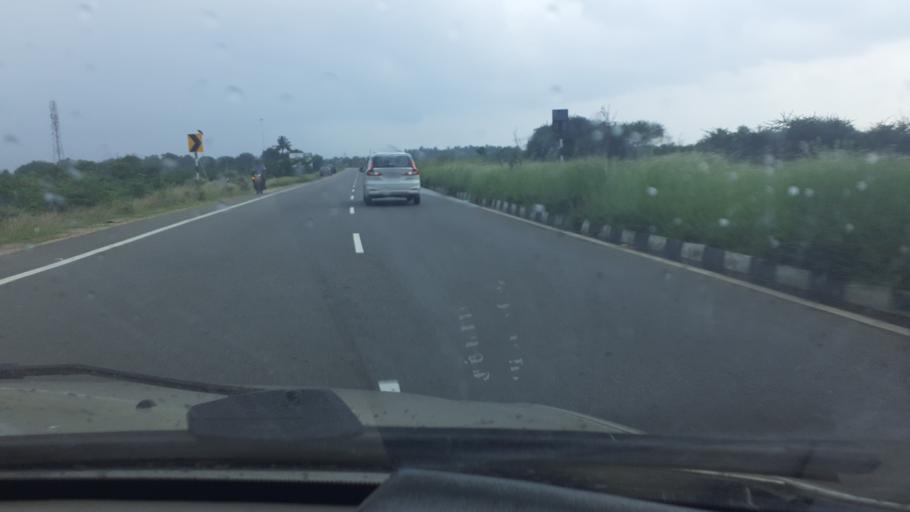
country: IN
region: Tamil Nadu
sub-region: Virudhunagar
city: Virudunagar
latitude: 9.6498
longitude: 77.9650
